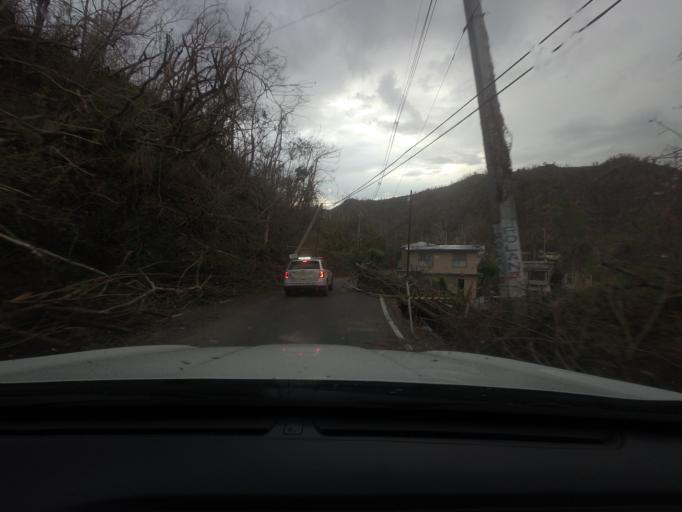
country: PR
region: Ciales
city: Ciales
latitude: 18.2901
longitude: -66.4833
